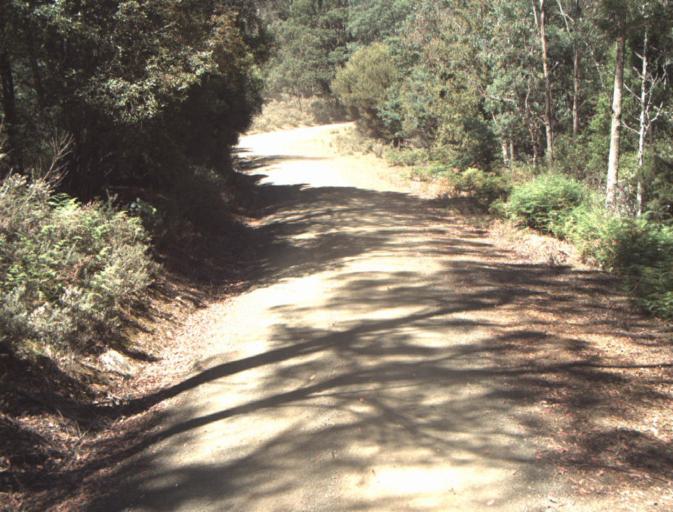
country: AU
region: Tasmania
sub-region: Dorset
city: Scottsdale
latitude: -41.3578
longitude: 147.4265
